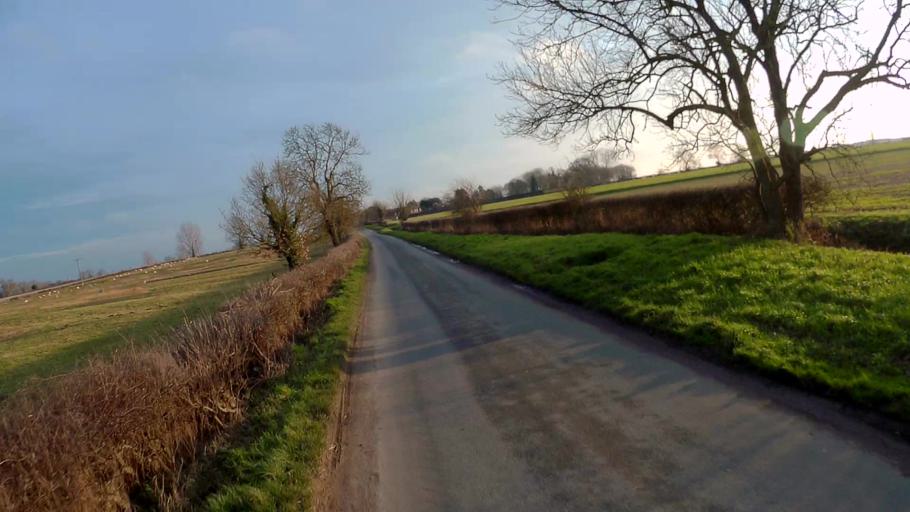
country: GB
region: England
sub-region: Lincolnshire
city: Bourne
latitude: 52.8080
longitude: -0.3967
